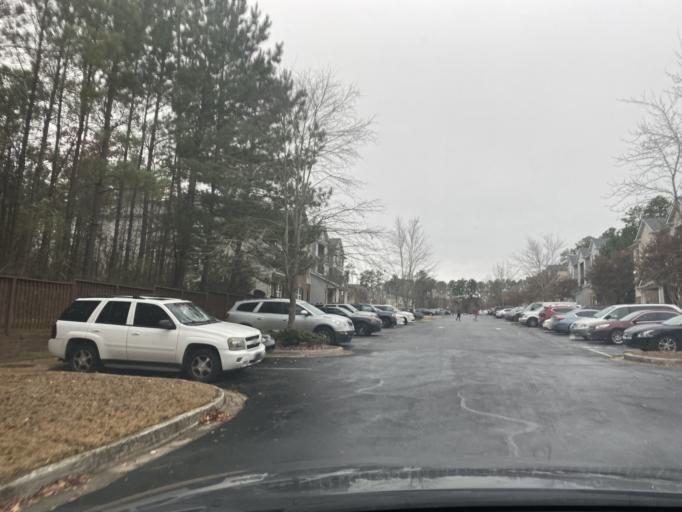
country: US
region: Georgia
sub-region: DeKalb County
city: Pine Mountain
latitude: 33.6996
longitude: -84.1521
